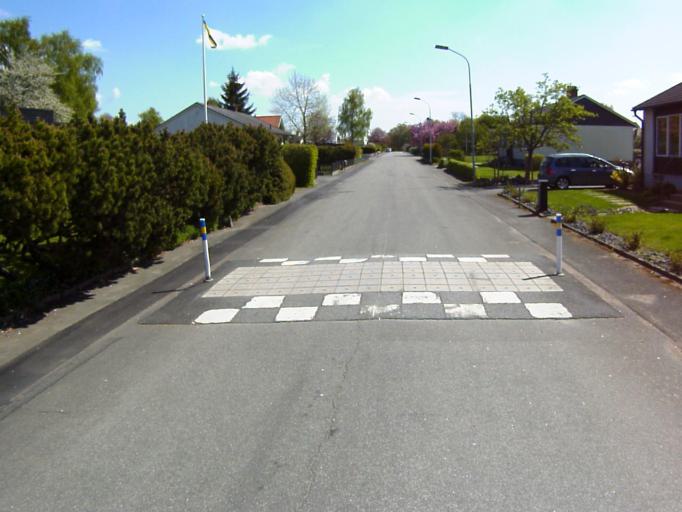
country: SE
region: Skane
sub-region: Kristianstads Kommun
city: Fjalkinge
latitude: 56.0148
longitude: 14.2284
